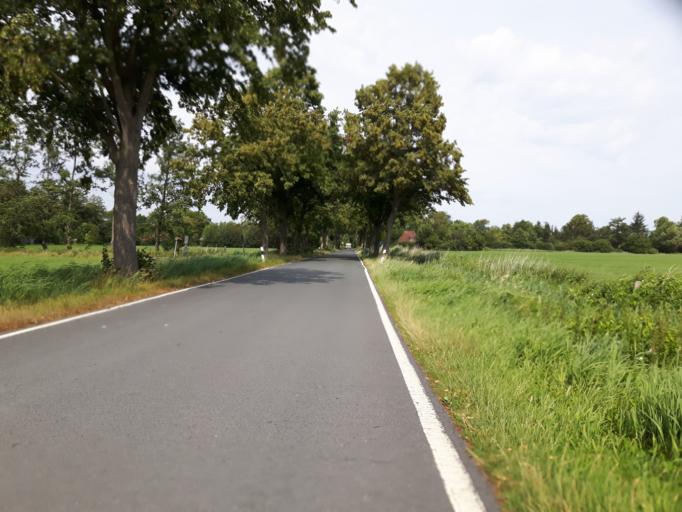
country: DE
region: Lower Saxony
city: Rastede
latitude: 53.3397
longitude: 8.2435
